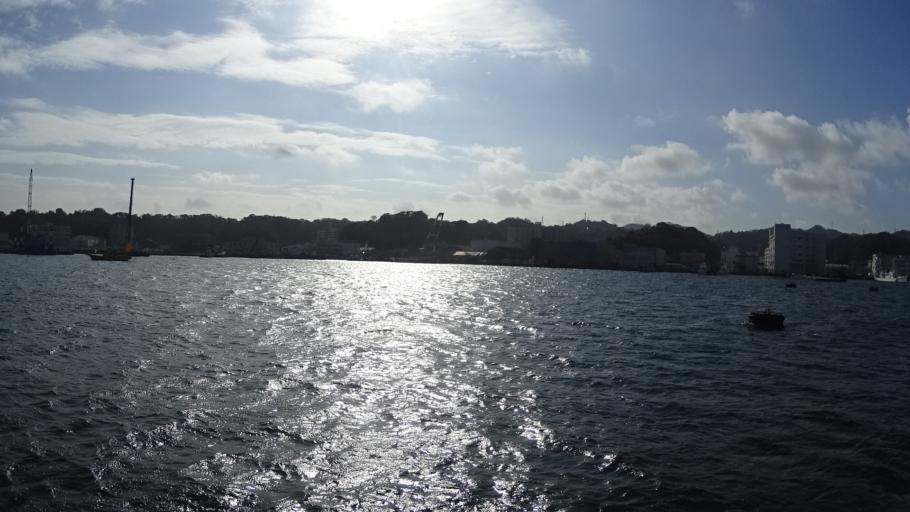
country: JP
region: Kanagawa
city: Yokosuka
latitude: 35.2991
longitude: 139.6377
